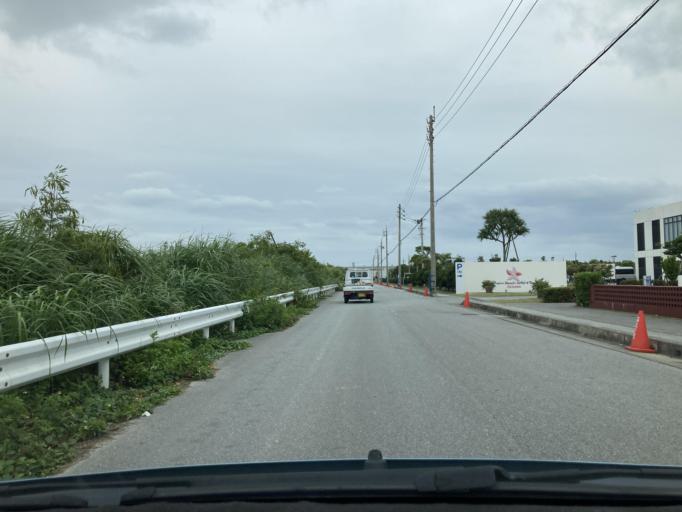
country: JP
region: Okinawa
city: Itoman
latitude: 26.1325
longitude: 127.6536
